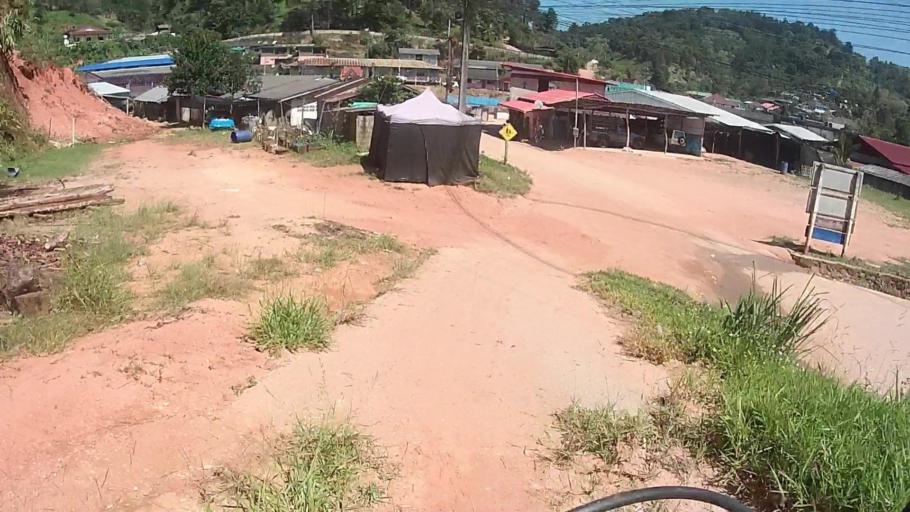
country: TH
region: Chiang Mai
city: Phrao
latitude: 19.4968
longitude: 99.3261
